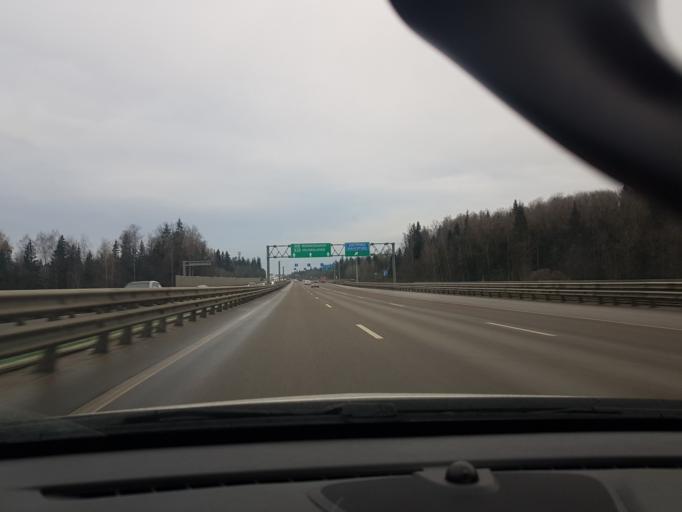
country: RU
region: Moskovskaya
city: Kostrovo
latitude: 55.8877
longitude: 36.6586
